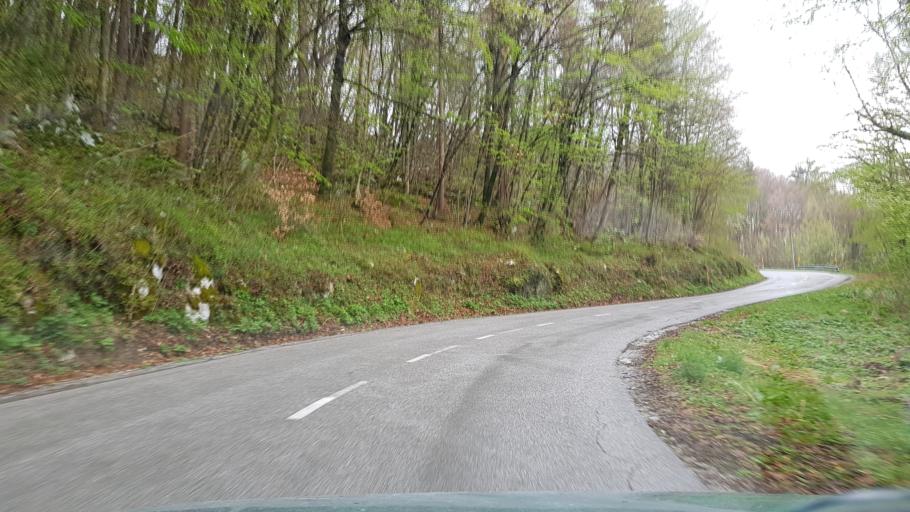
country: SI
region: Tolmin
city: Tolmin
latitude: 46.1114
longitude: 13.8250
